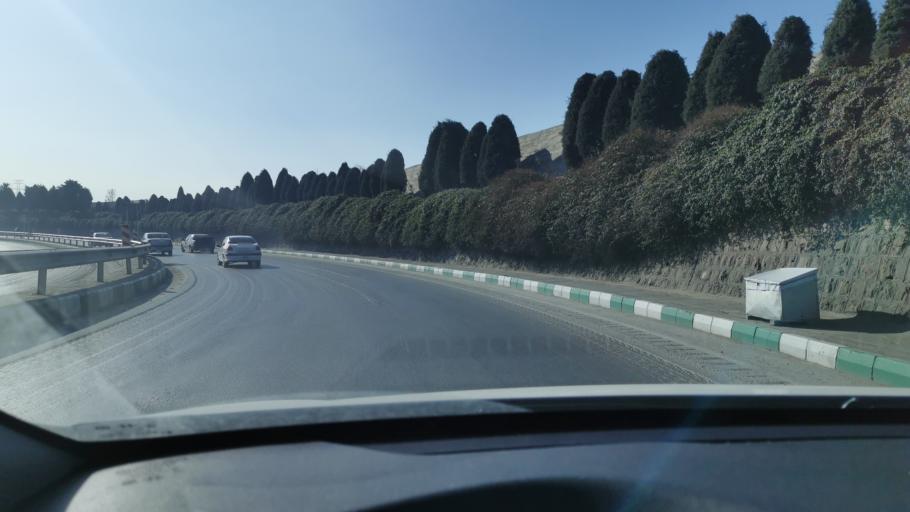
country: IR
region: Razavi Khorasan
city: Mashhad
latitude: 36.2632
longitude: 59.5805
